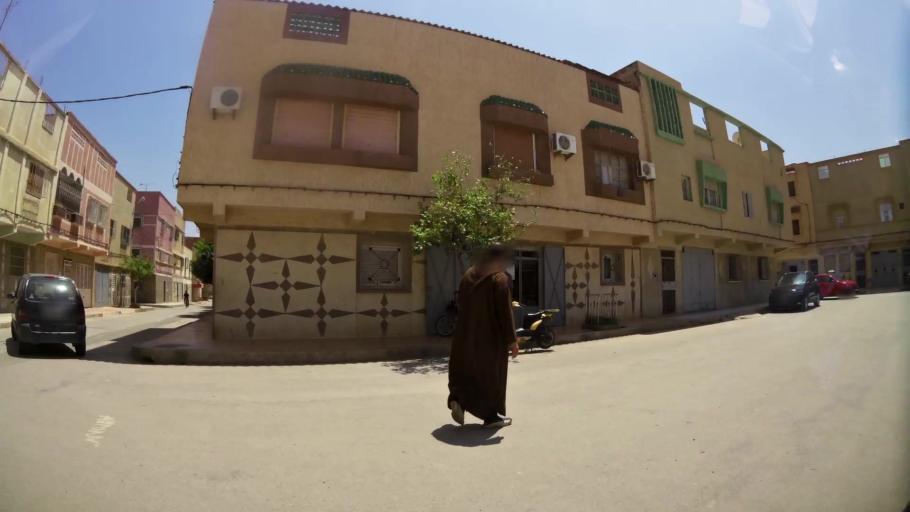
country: MA
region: Oriental
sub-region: Oujda-Angad
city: Oujda
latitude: 34.6993
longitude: -1.8968
